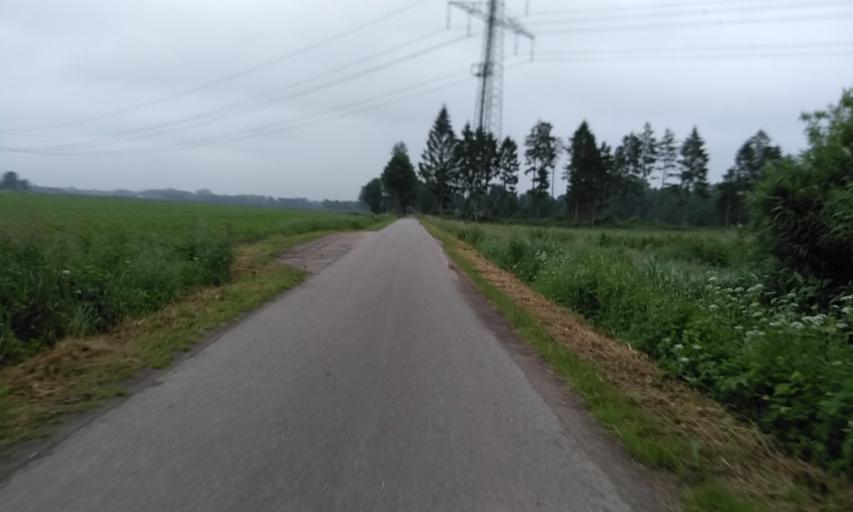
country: DE
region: Lower Saxony
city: Horneburg
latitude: 53.5230
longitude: 9.5697
